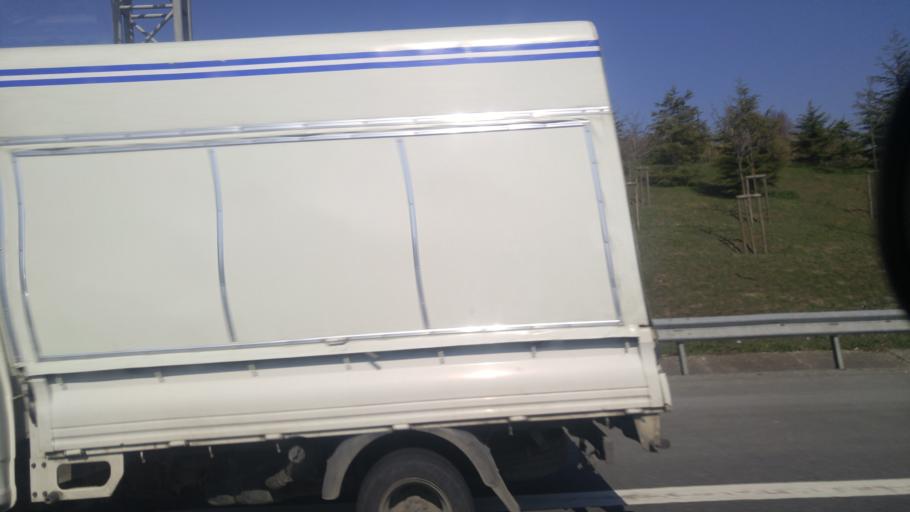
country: TR
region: Istanbul
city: Selimpasa
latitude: 41.0679
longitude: 28.3906
